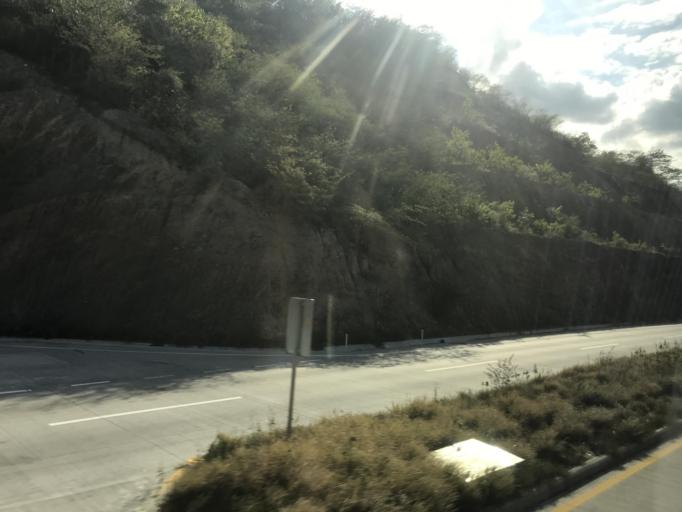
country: GT
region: El Progreso
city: Guastatoya
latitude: 14.8541
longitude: -90.0984
